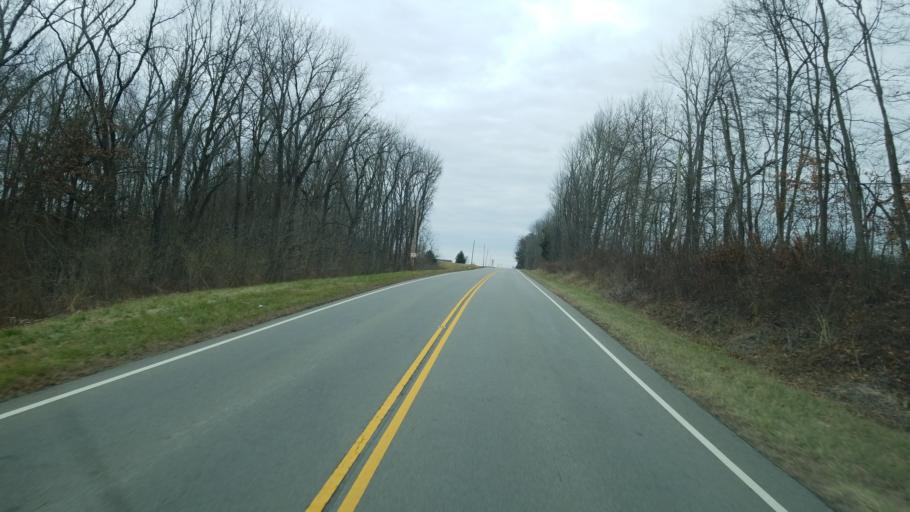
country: US
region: Ohio
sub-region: Highland County
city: Hillsboro
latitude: 39.2163
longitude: -83.4784
